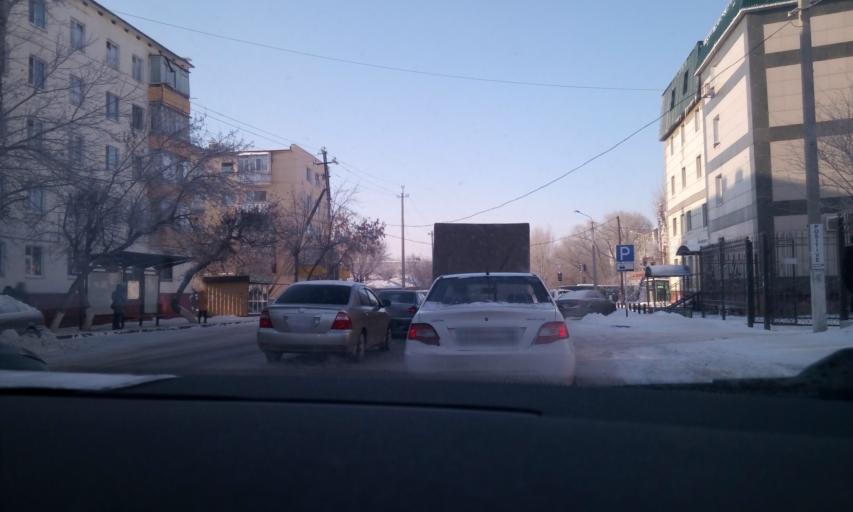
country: KZ
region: Astana Qalasy
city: Astana
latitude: 51.1796
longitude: 71.4248
